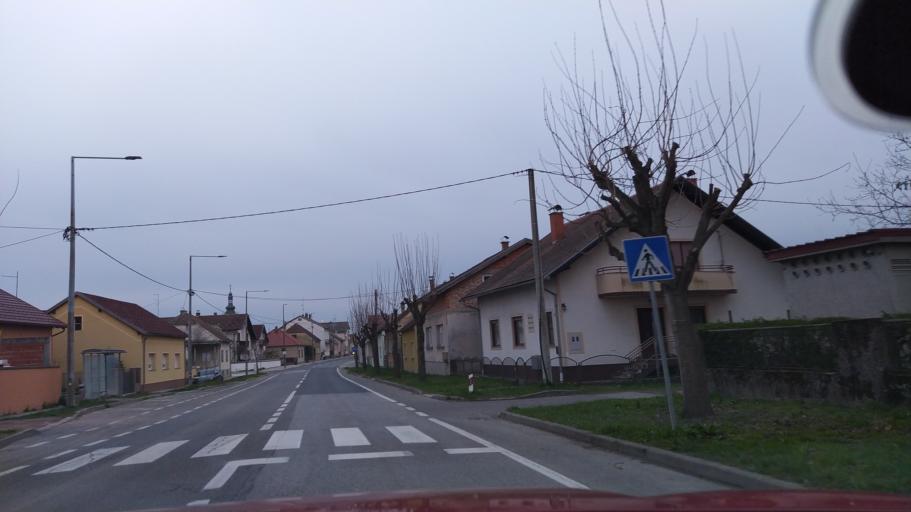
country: HR
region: Varazdinska
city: Ludbreg
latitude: 46.2496
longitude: 16.6117
